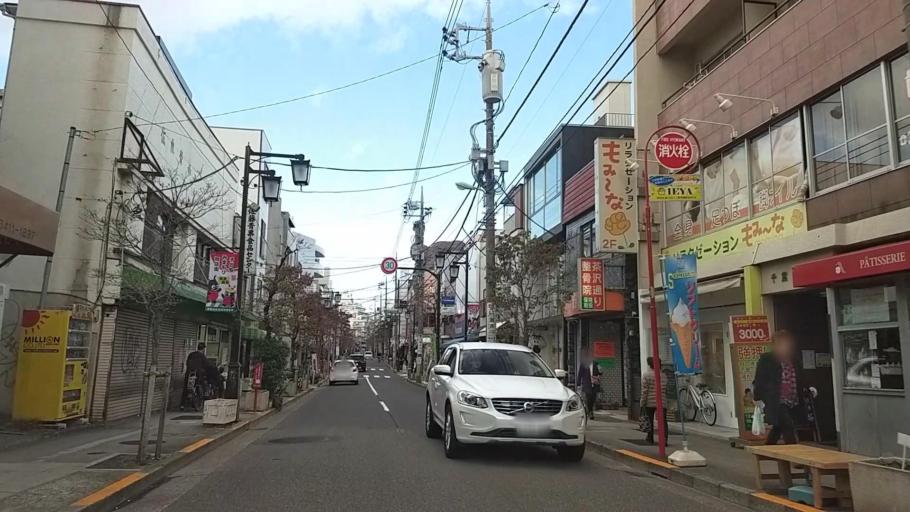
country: JP
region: Tokyo
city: Tokyo
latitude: 35.6470
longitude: 139.6695
